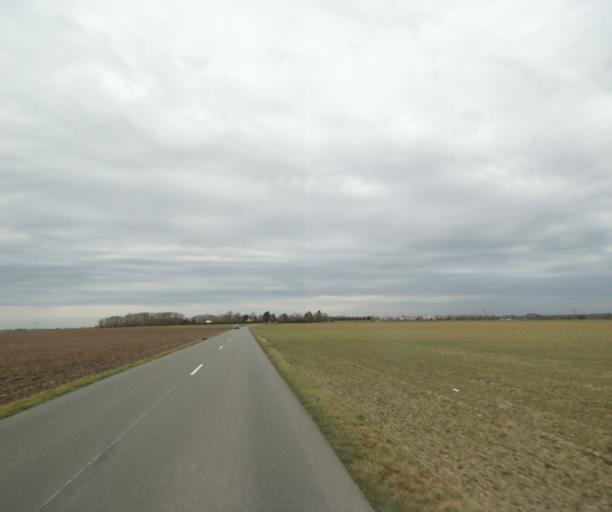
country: FR
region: Nord-Pas-de-Calais
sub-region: Departement du Nord
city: Saultain
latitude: 50.3595
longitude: 3.5798
